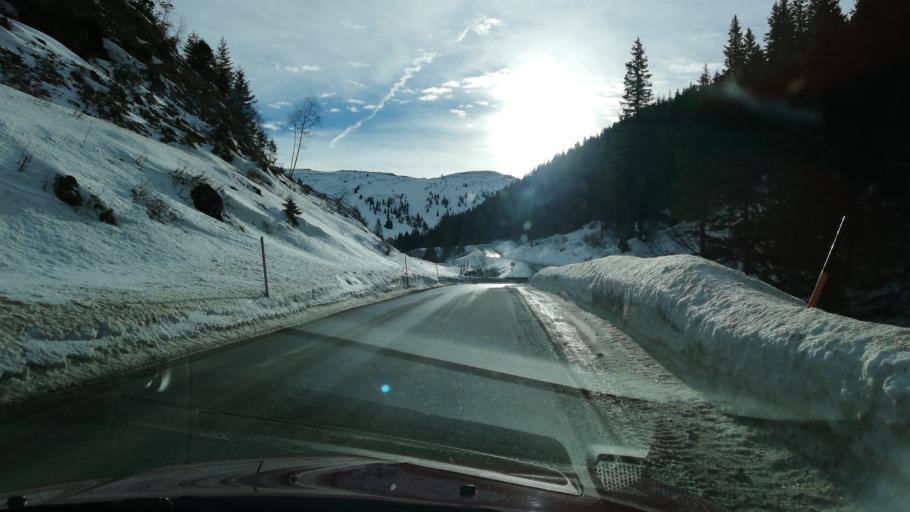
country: AT
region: Styria
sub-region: Politischer Bezirk Liezen
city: Donnersbach
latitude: 47.4096
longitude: 14.1876
